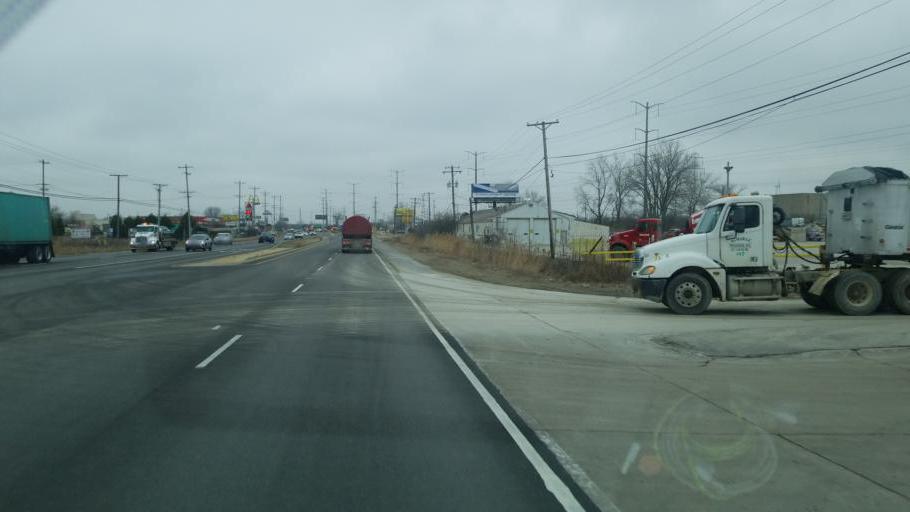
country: US
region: Illinois
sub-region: Lake County
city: Knollwood
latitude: 42.3010
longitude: -87.8756
